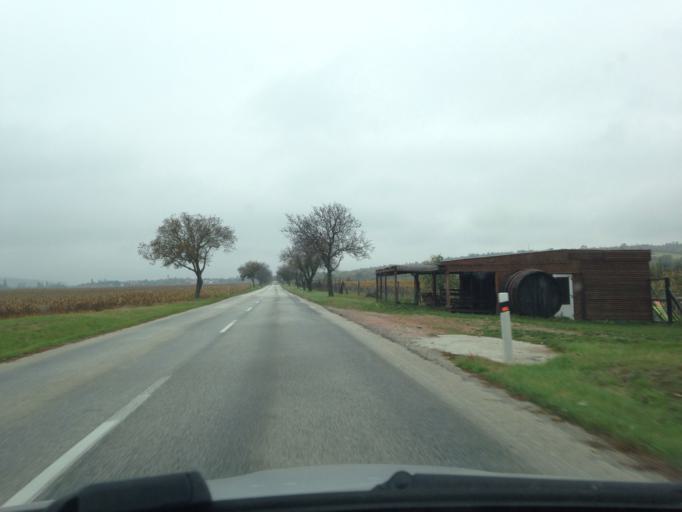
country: HU
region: Komarom-Esztergom
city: Nyergesujfalu
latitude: 47.8365
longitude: 18.5415
